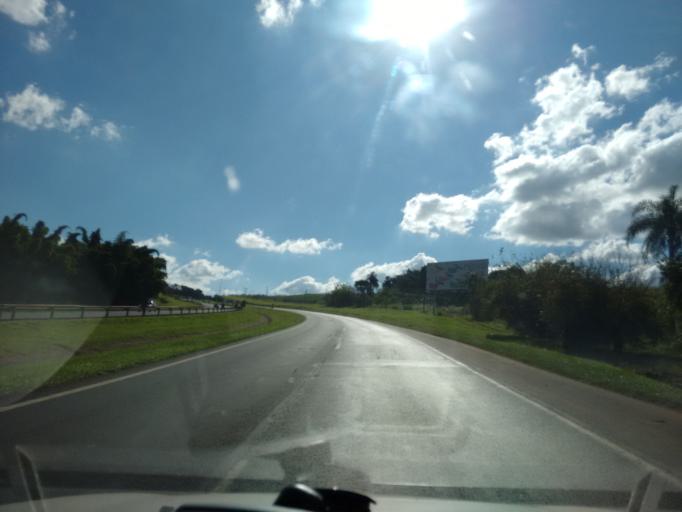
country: BR
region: Sao Paulo
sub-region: Araraquara
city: Araraquara
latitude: -21.8771
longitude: -48.0922
